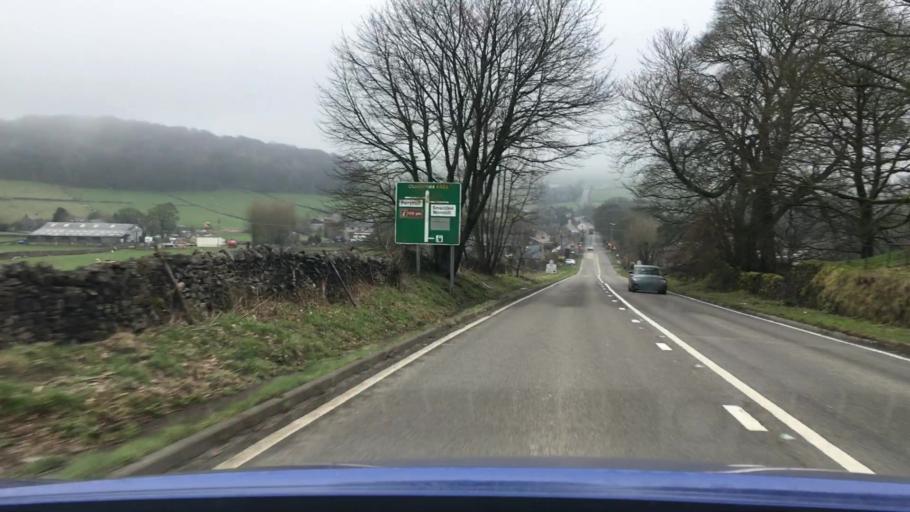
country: GB
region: England
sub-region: Derbyshire
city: High Peak
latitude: 53.3120
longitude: -1.8355
